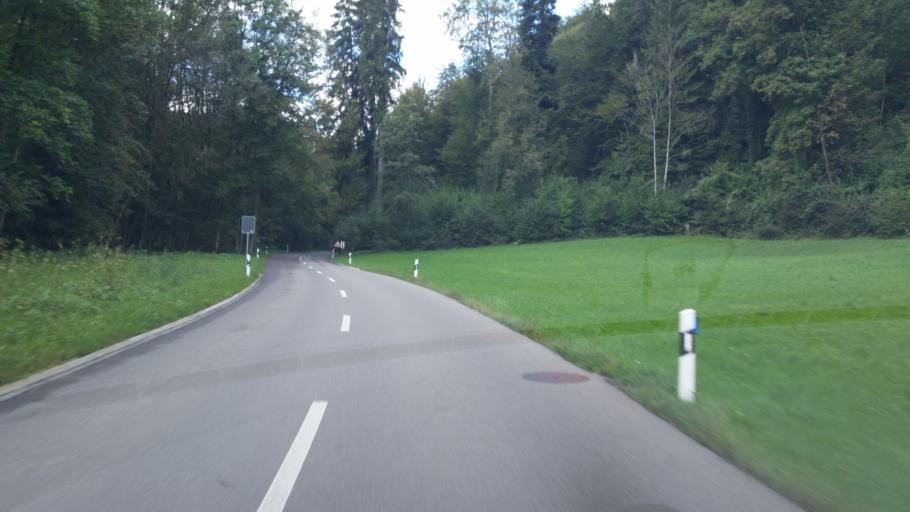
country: CH
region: Zurich
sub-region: Bezirk Affoltern
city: Affoltern / Sonnenberg
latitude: 47.2641
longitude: 8.4712
